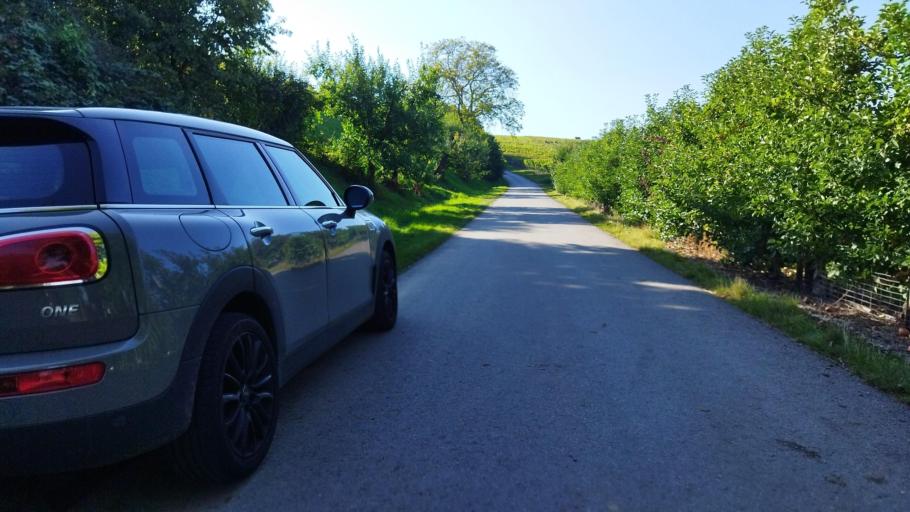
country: DE
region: Baden-Wuerttemberg
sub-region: Regierungsbezirk Stuttgart
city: Erligheim
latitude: 49.0182
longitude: 9.0823
